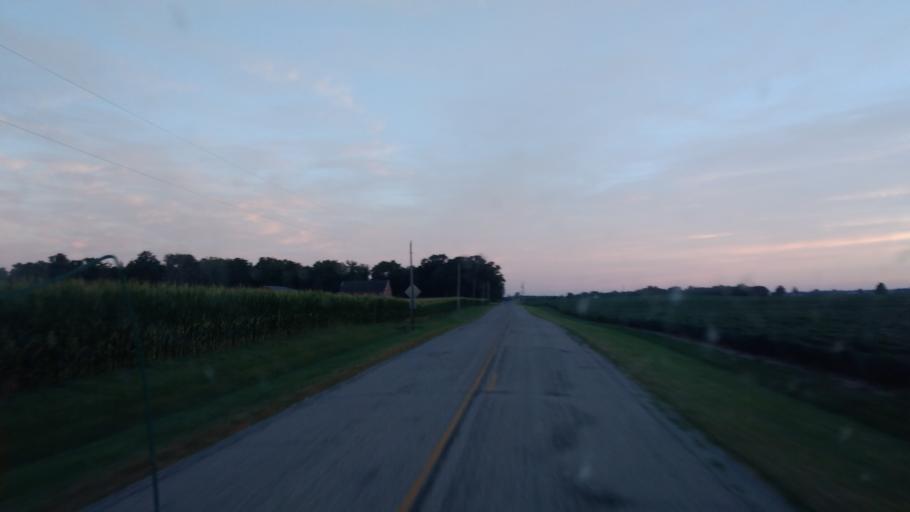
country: US
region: Indiana
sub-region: Wells County
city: Bluffton
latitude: 40.6720
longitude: -85.1275
